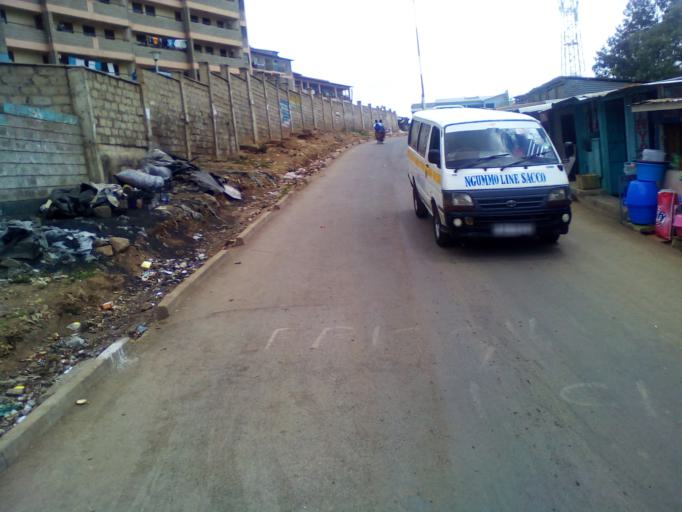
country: KE
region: Nairobi Area
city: Nairobi
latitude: -1.3157
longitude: 36.8022
